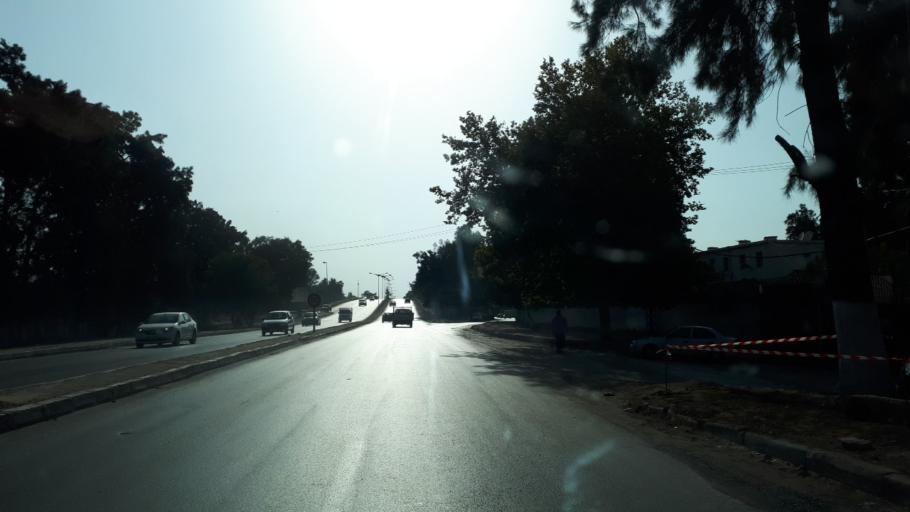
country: DZ
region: Alger
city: Dar el Beida
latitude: 36.7280
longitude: 3.2153
